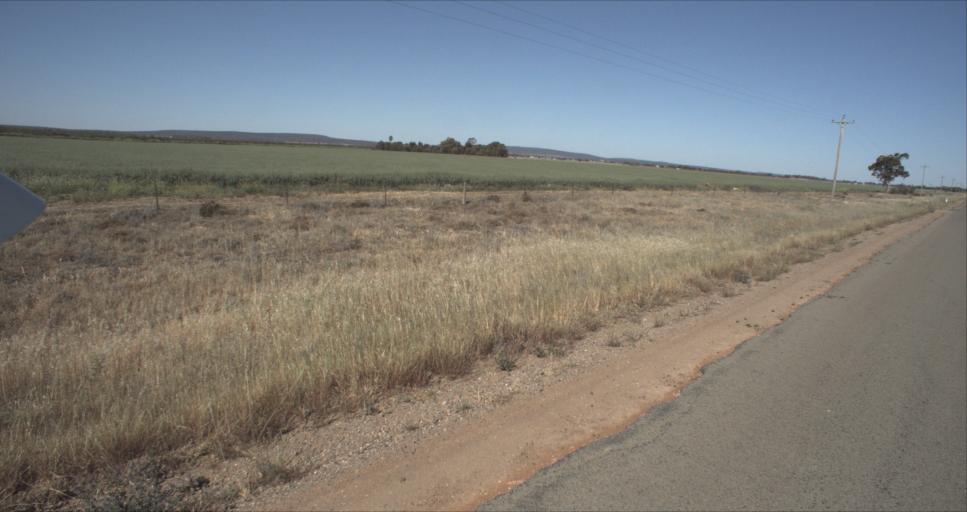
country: AU
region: New South Wales
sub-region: Leeton
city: Leeton
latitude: -34.4819
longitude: 146.3724
